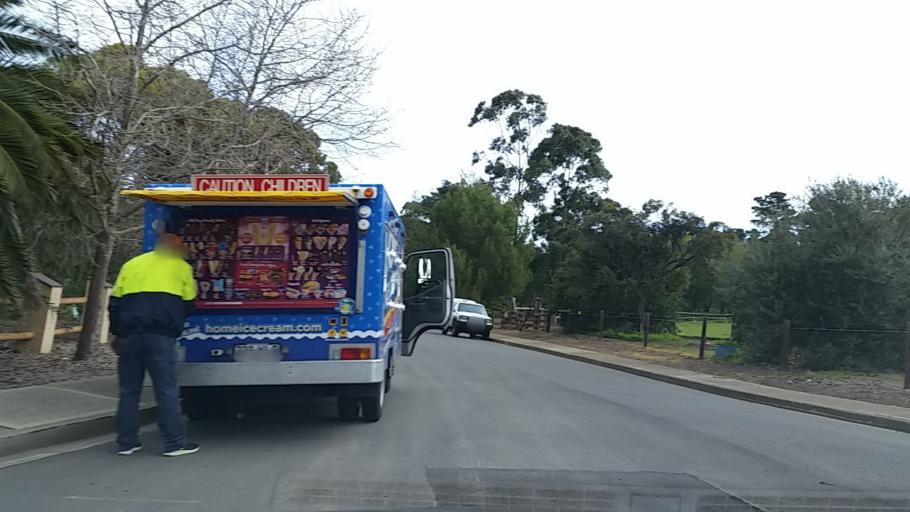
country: AU
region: South Australia
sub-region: Marion
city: Trott Park
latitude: -35.0632
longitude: 138.5383
